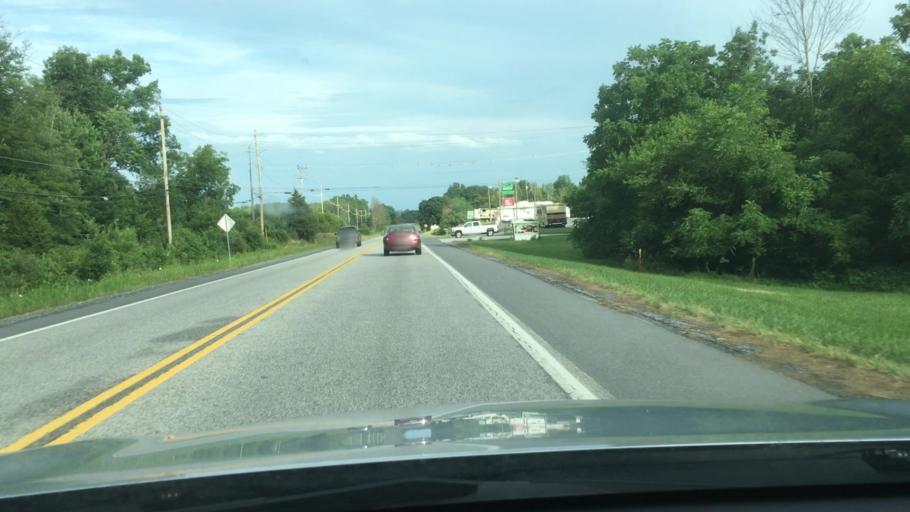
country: US
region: Pennsylvania
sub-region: York County
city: Dillsburg
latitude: 40.0908
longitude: -76.9518
